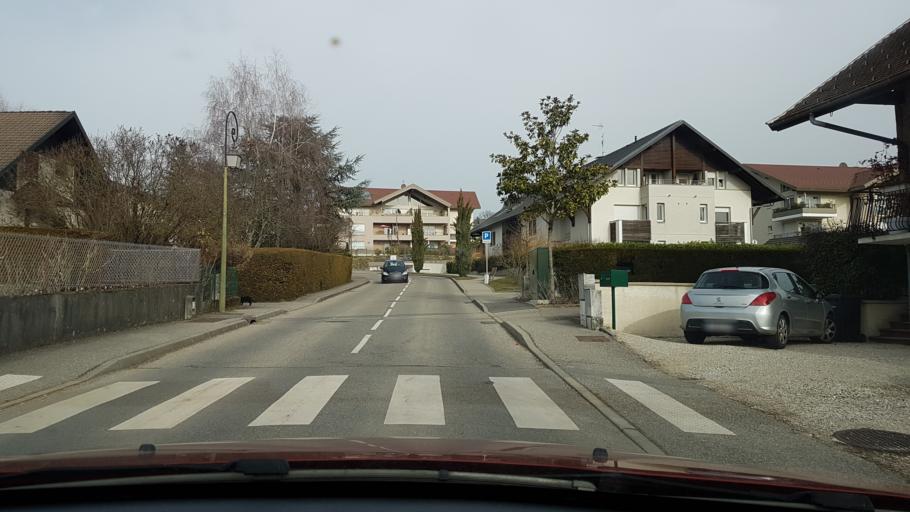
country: FR
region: Rhone-Alpes
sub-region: Departement de la Haute-Savoie
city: Metz-Tessy
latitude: 45.9414
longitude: 6.1051
